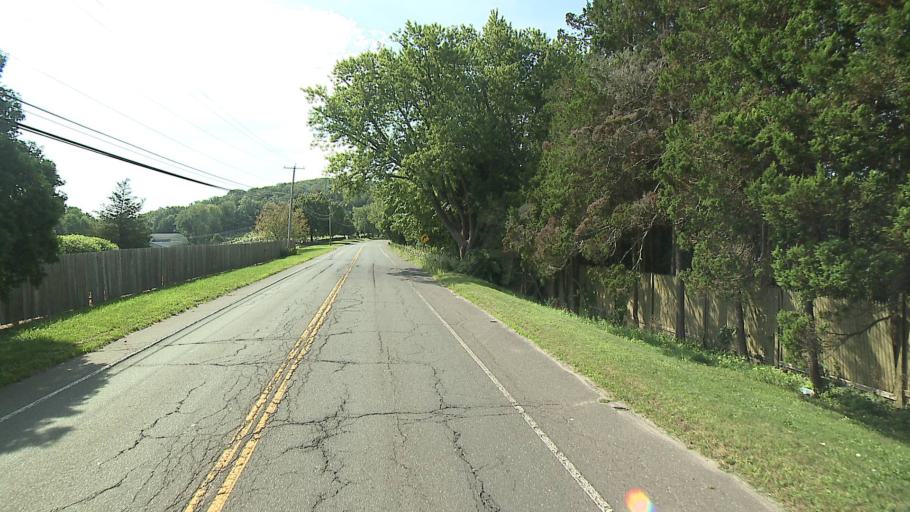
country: US
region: New York
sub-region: Putnam County
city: Putnam Lake
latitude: 41.4821
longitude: -73.4974
